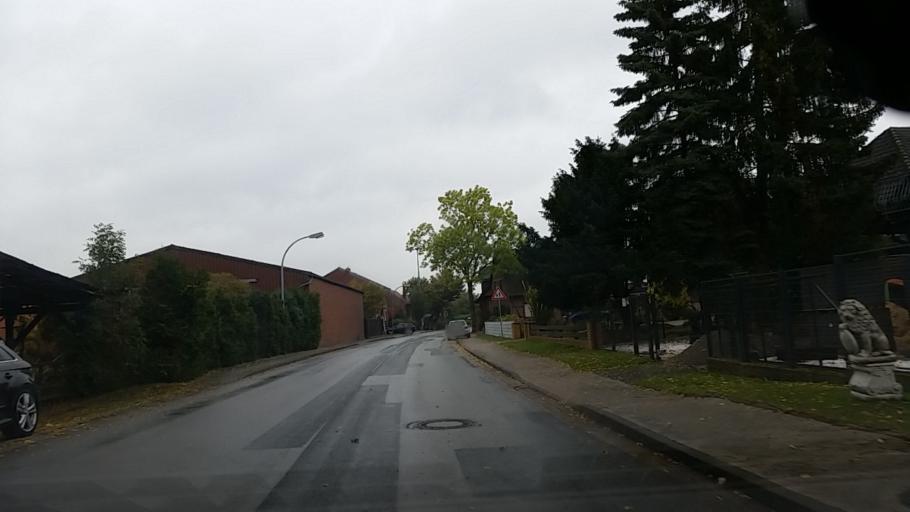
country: DE
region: Lower Saxony
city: Tiddische
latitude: 52.4987
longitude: 10.8009
